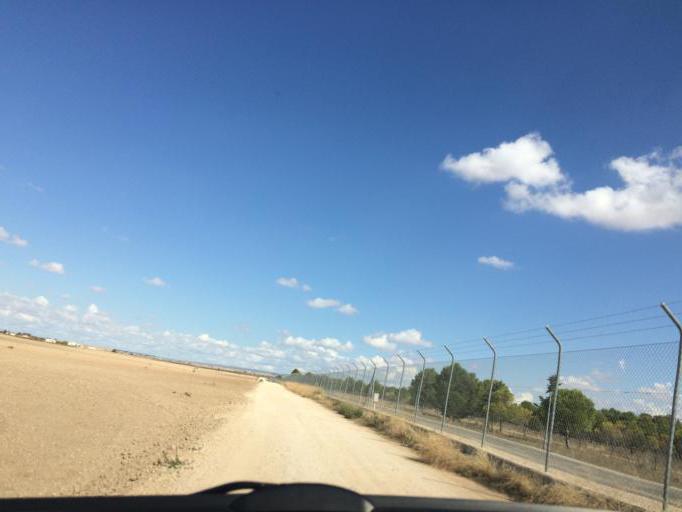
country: ES
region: Castille-La Mancha
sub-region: Provincia de Albacete
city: Albacete
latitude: 38.9578
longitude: -1.8586
